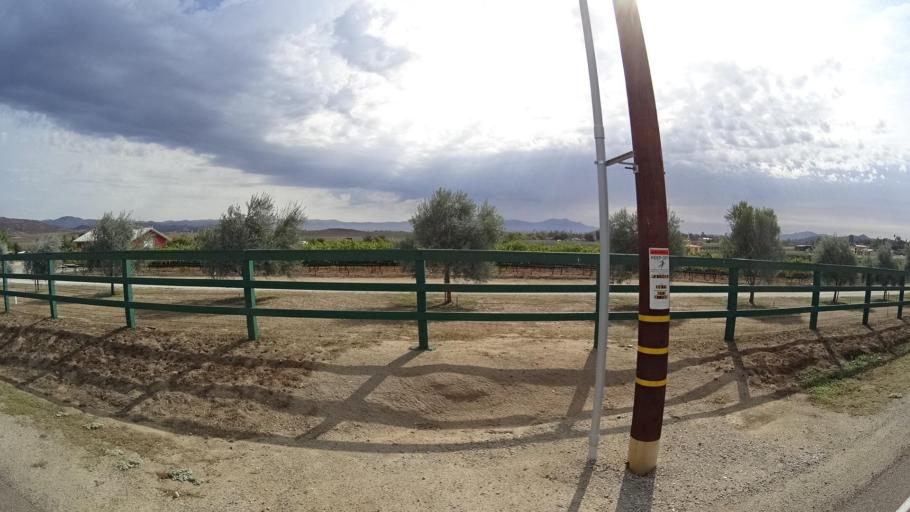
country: US
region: California
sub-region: San Diego County
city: San Pasqual
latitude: 33.0303
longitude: -116.9361
